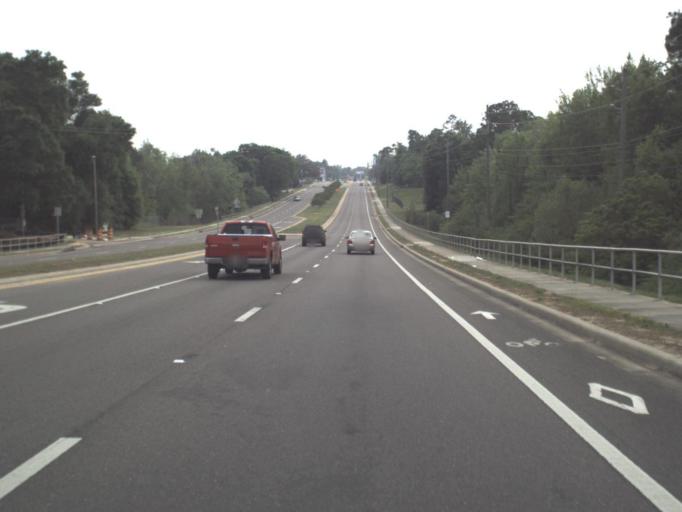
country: US
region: Florida
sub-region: Santa Rosa County
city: Milton
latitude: 30.6392
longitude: -87.0556
